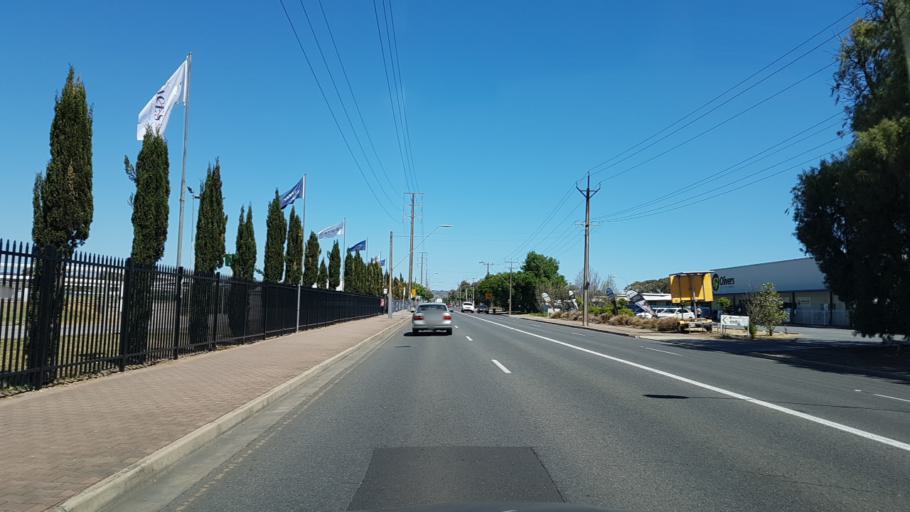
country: AU
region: South Australia
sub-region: Holdfast Bay
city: Glenelg East
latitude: -34.9786
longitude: 138.5381
